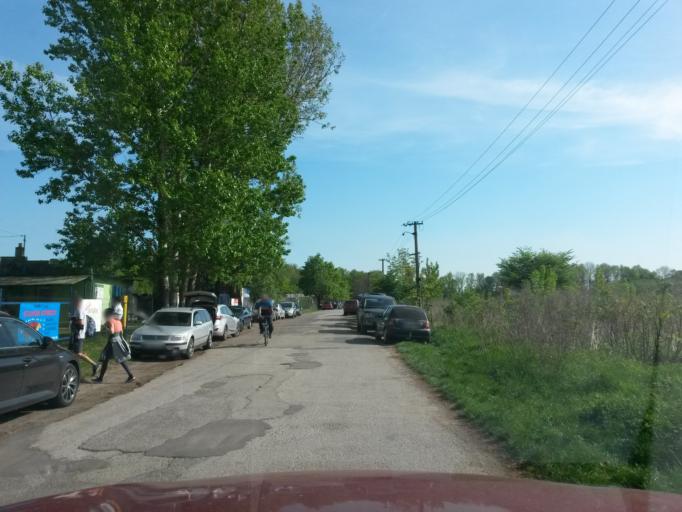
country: SK
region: Kosicky
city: Kosice
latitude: 48.7544
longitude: 21.2522
